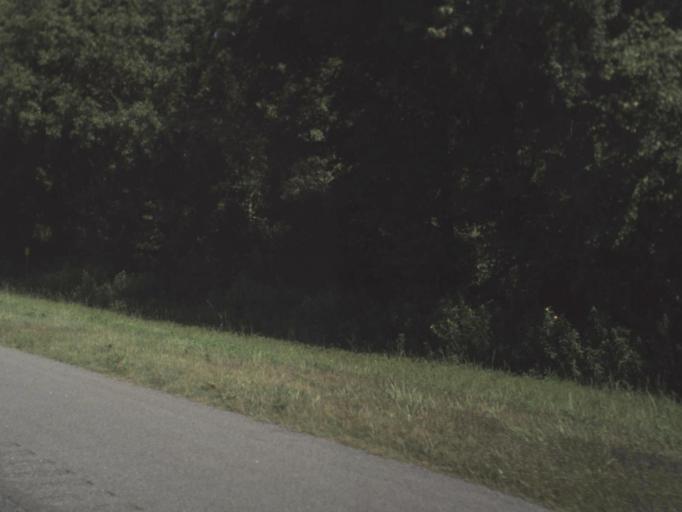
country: US
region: Florida
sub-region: Suwannee County
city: Live Oak
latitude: 30.3516
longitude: -83.0227
